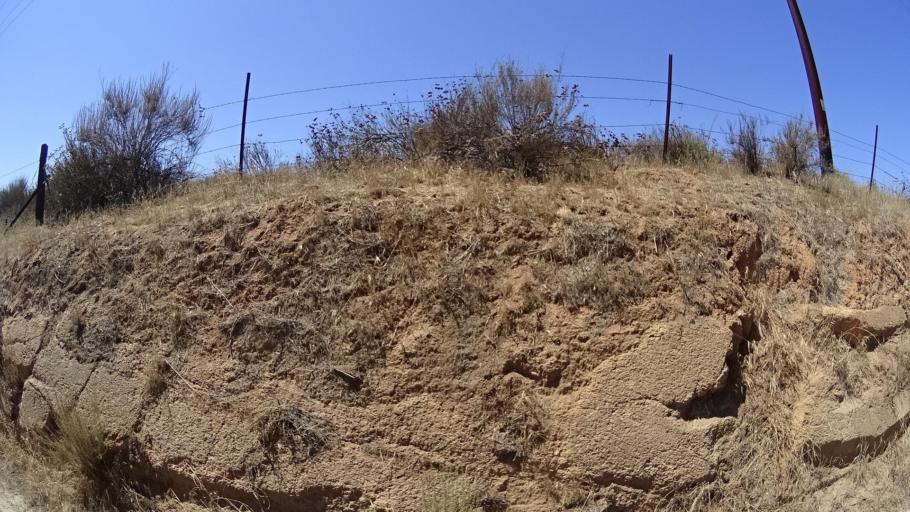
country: US
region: California
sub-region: San Diego County
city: Hidden Meadows
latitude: 33.2909
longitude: -117.0814
